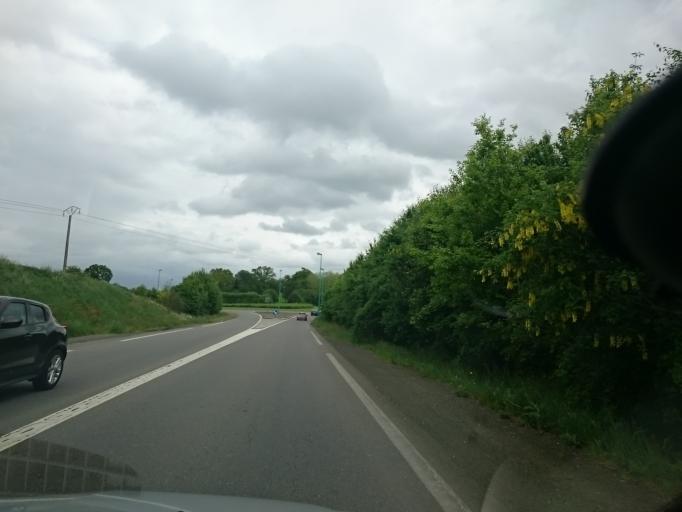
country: FR
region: Brittany
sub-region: Departement d'Ille-et-Vilaine
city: Saint-Brice-en-Cogles
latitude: 48.3999
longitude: -1.3743
